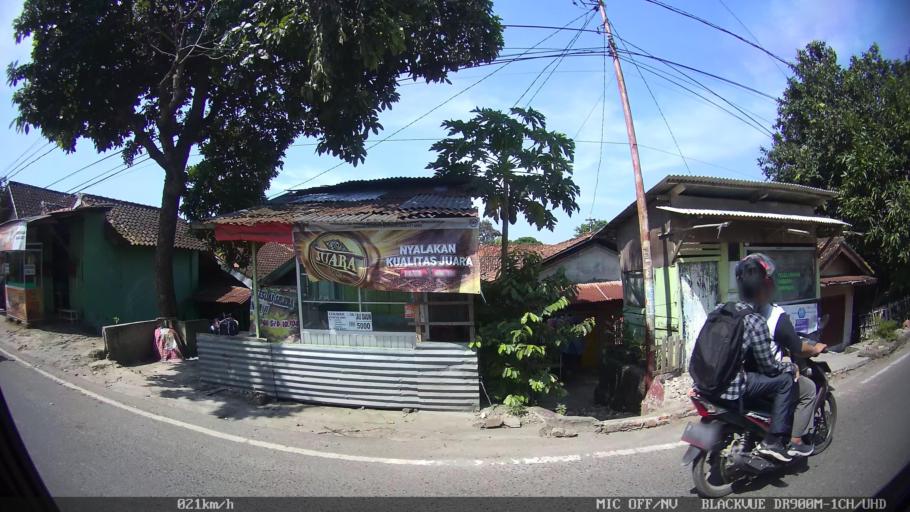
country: ID
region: Lampung
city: Kedaton
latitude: -5.3731
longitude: 105.2536
